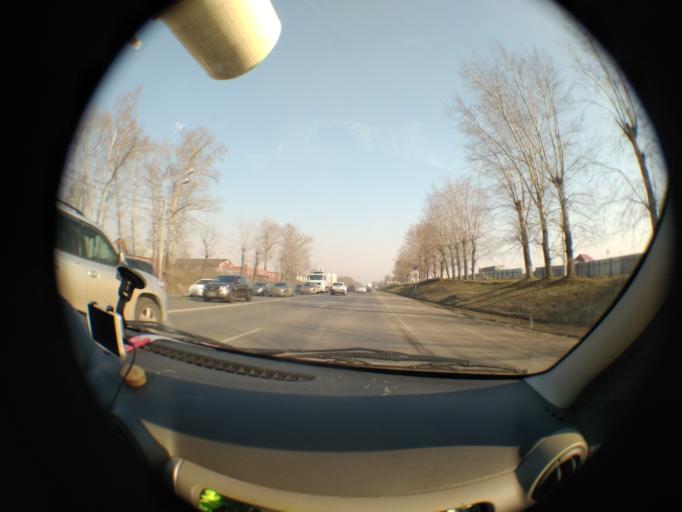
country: RU
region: Moskovskaya
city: Oktyabr'skiy
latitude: 55.5965
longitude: 37.9897
